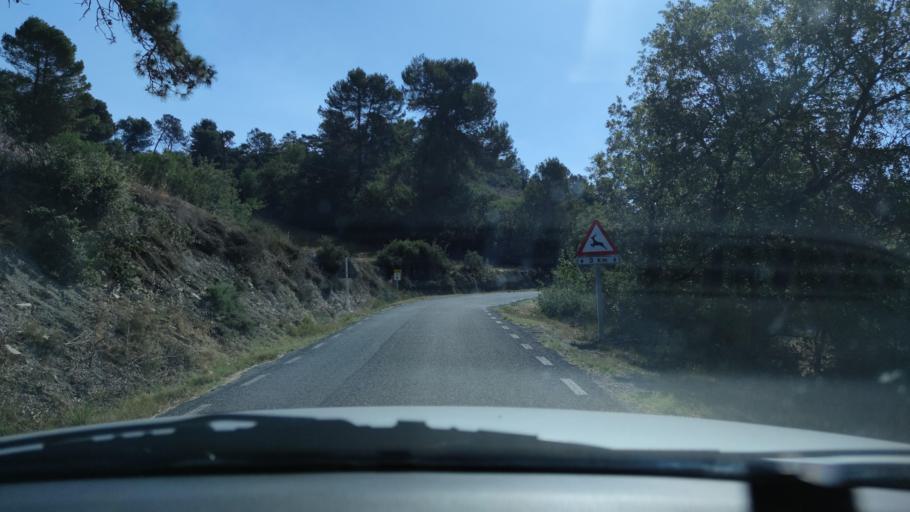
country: ES
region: Catalonia
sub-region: Provincia de Barcelona
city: Pujalt
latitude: 41.7097
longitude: 1.3755
